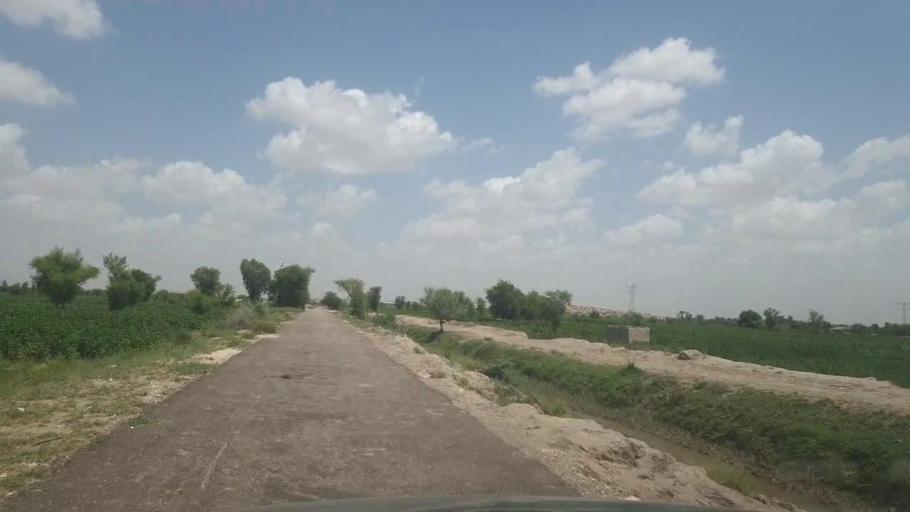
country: PK
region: Sindh
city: Kot Diji
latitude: 27.2343
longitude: 69.0370
